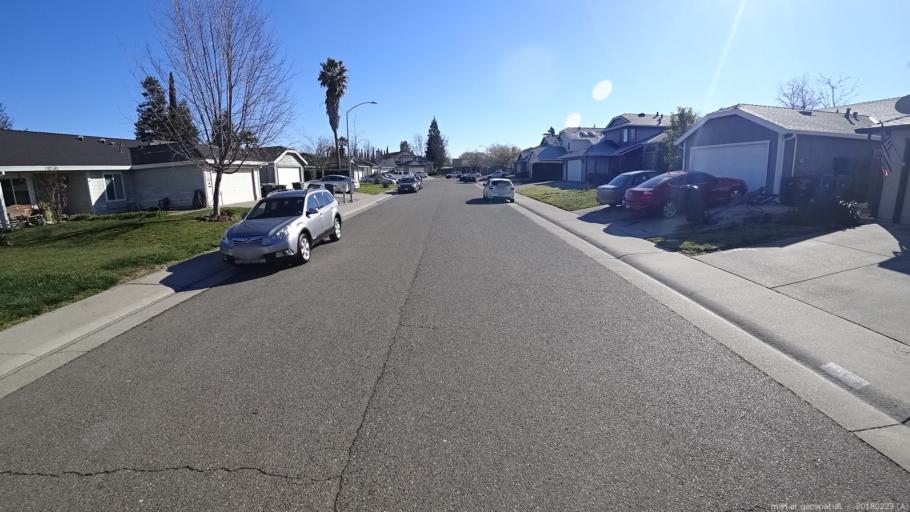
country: US
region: California
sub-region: Sacramento County
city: North Highlands
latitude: 38.7103
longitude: -121.3681
